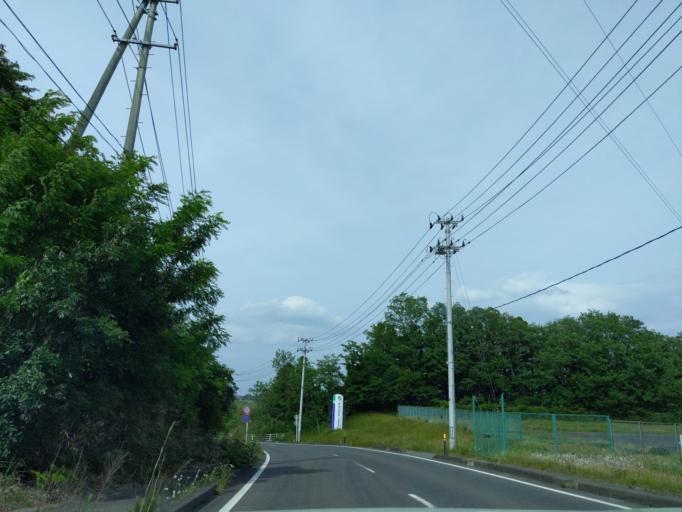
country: JP
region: Fukushima
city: Koriyama
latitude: 37.4517
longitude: 140.3117
